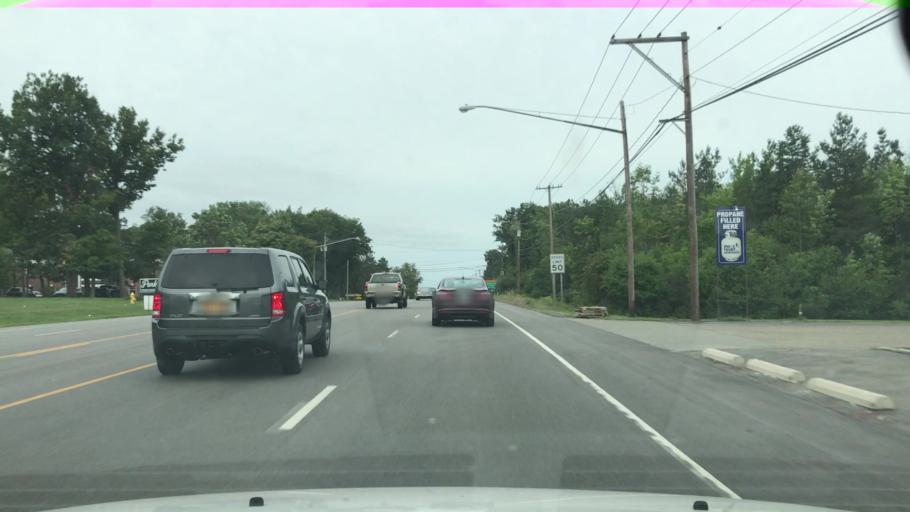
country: US
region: New York
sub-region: Erie County
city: Orchard Park
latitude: 42.8020
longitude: -78.7416
